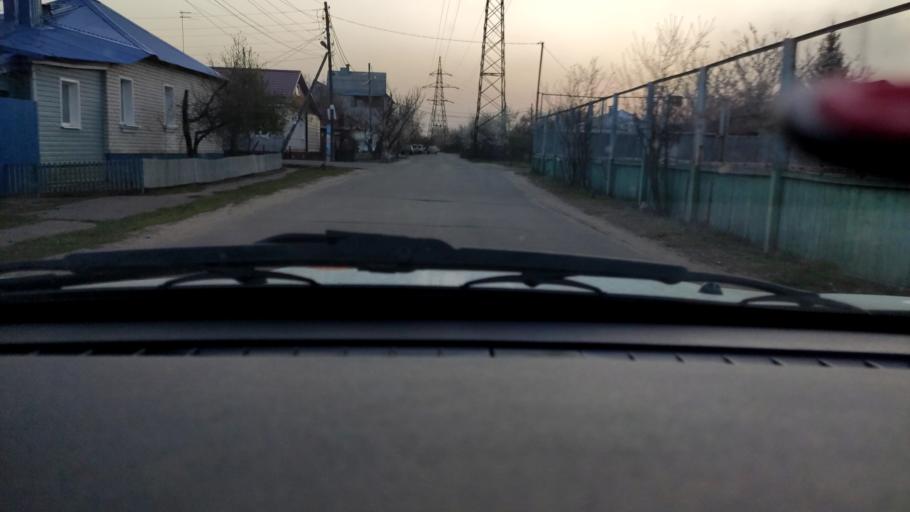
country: RU
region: Voronezj
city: Voronezh
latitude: 51.6249
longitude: 39.1735
